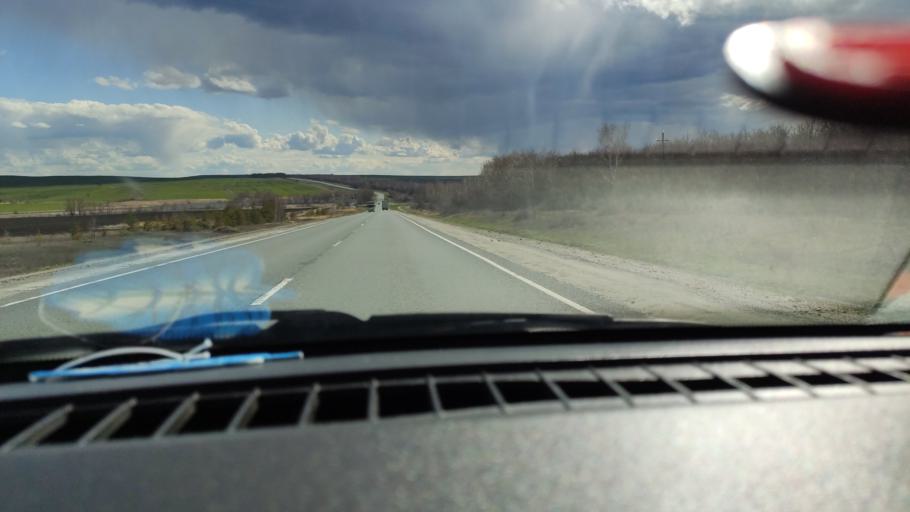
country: RU
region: Saratov
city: Alekseyevka
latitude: 52.2497
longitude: 47.9114
